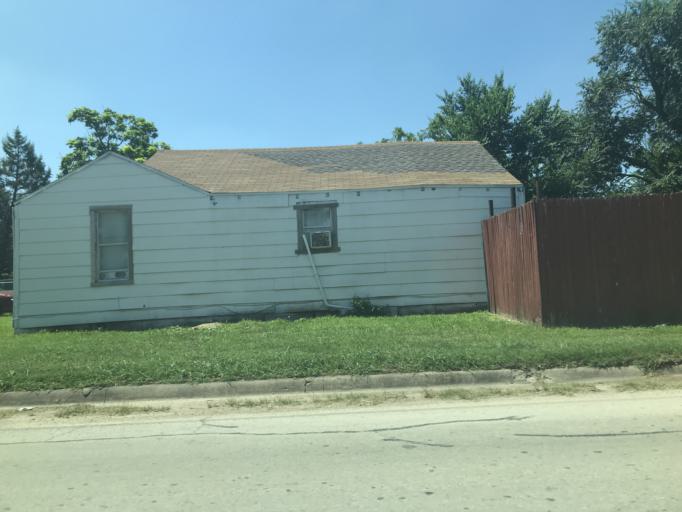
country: US
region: Texas
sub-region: Taylor County
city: Abilene
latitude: 32.4632
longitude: -99.7468
